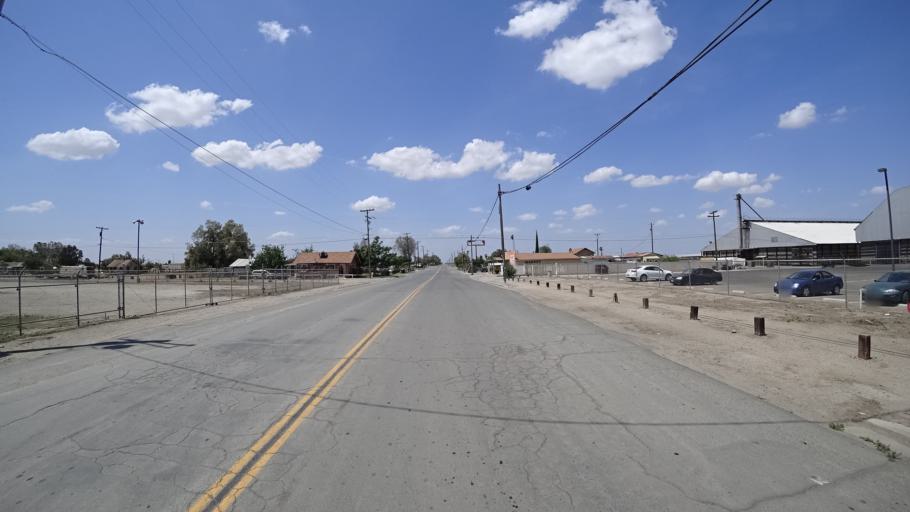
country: US
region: California
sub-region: Kings County
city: Stratford
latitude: 36.1894
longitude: -119.8249
